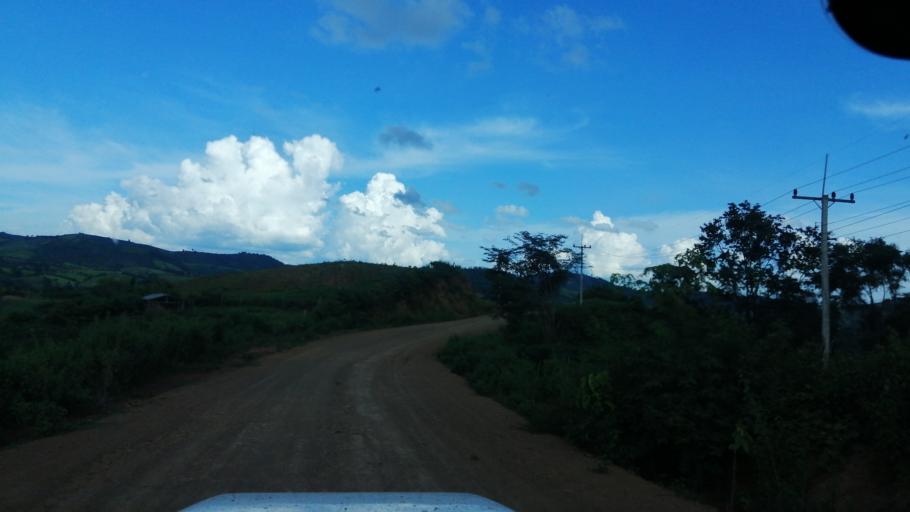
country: LA
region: Xiagnabouli
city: Muang Kenthao
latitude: 17.8535
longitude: 101.2377
